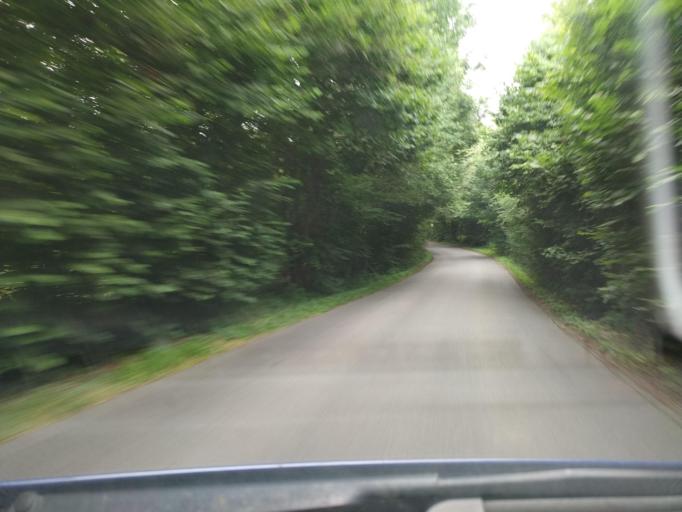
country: DE
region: Schleswig-Holstein
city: Neuberend
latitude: 54.5184
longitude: 9.5195
